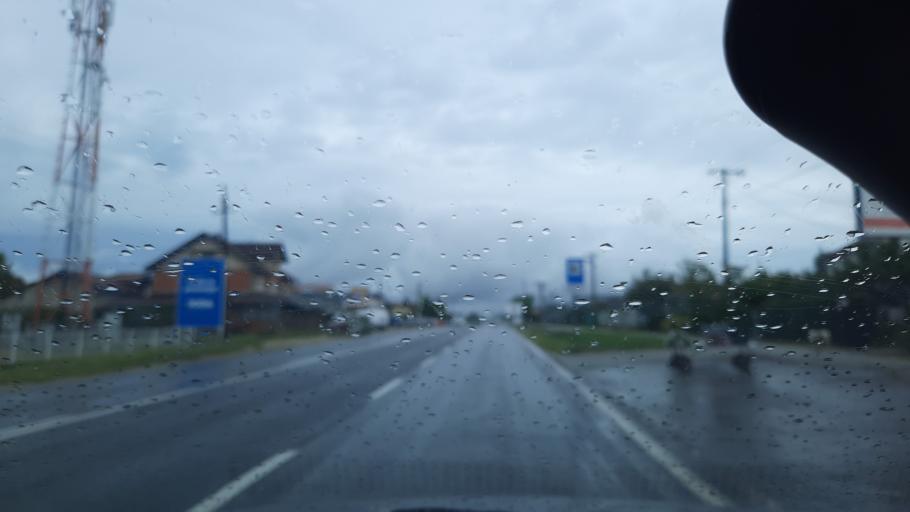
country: RS
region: Central Serbia
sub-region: Sumadijski Okrug
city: Kragujevac
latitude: 43.9893
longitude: 20.8519
